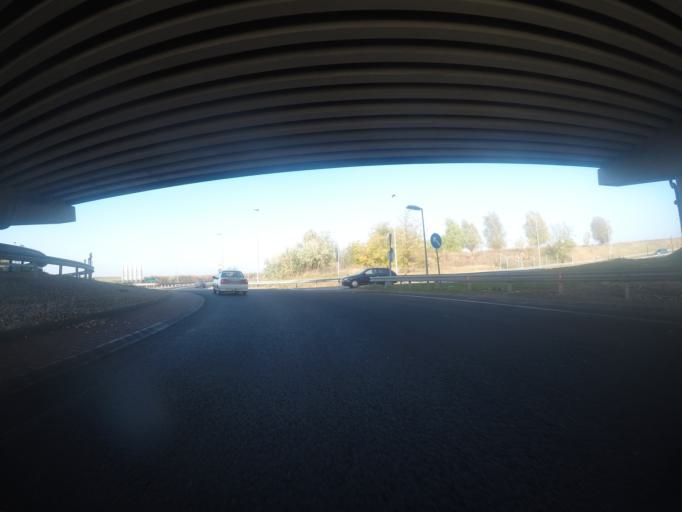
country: HU
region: Fejer
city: Baracs
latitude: 46.9106
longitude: 18.9265
